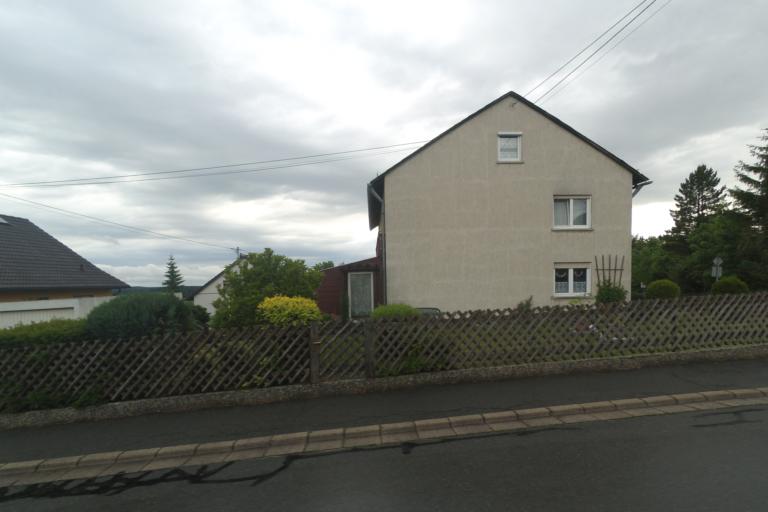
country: DE
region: Bavaria
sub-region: Upper Franconia
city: Schauenstein
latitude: 50.2796
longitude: 11.7460
